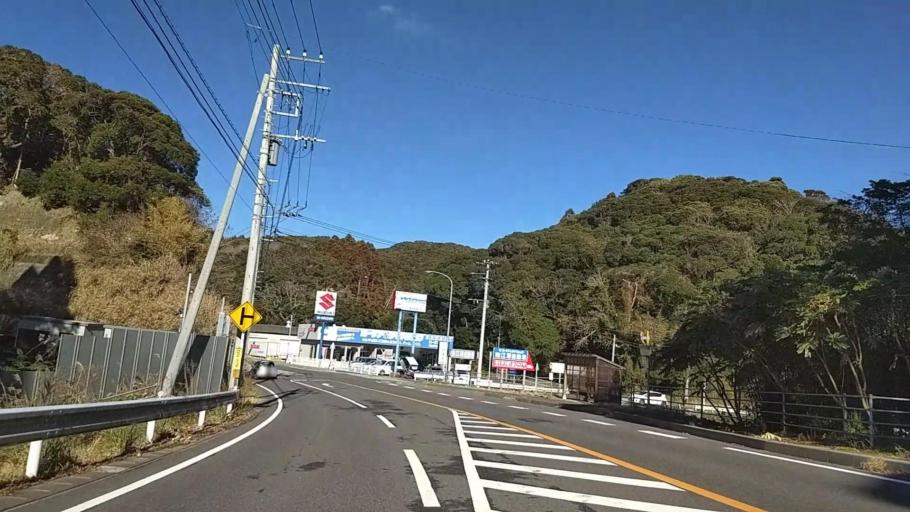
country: JP
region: Chiba
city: Katsuura
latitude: 35.1588
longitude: 140.3271
